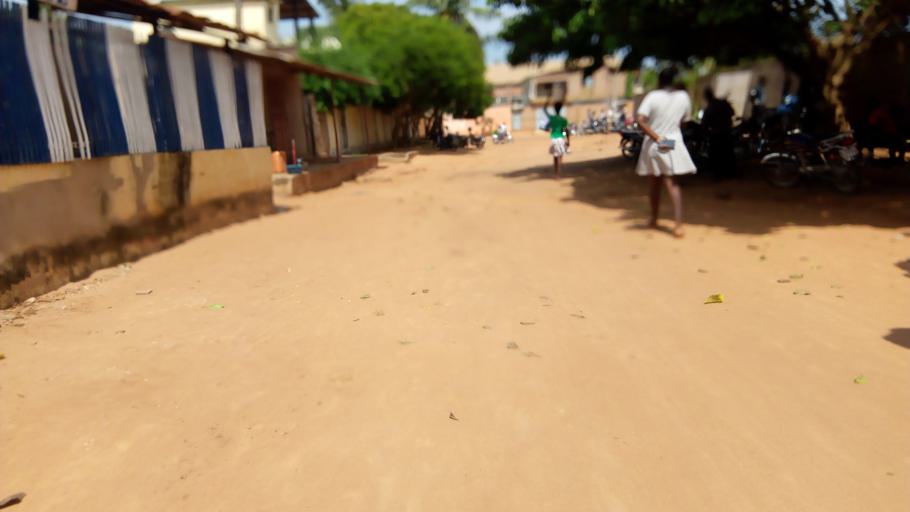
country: TG
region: Maritime
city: Lome
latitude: 6.1850
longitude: 1.1776
